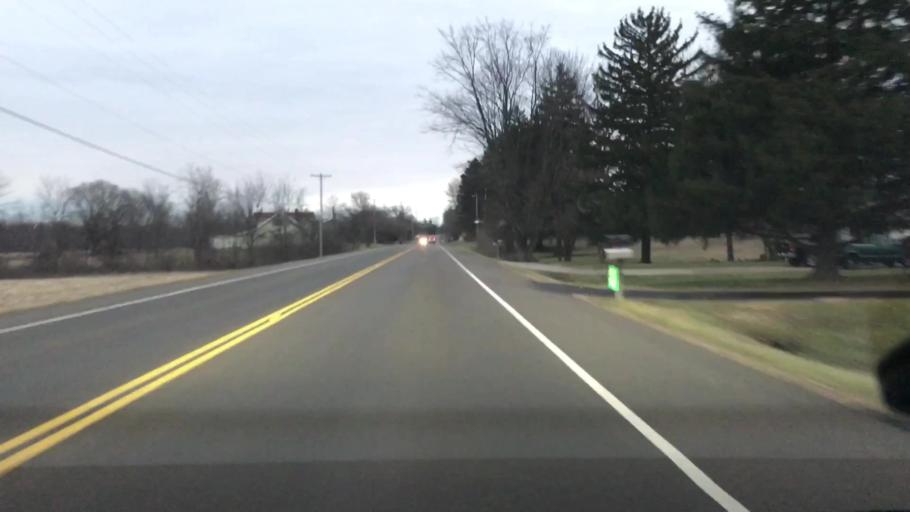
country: US
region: Ohio
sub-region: Clark County
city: Springfield
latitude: 39.9088
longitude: -83.8704
